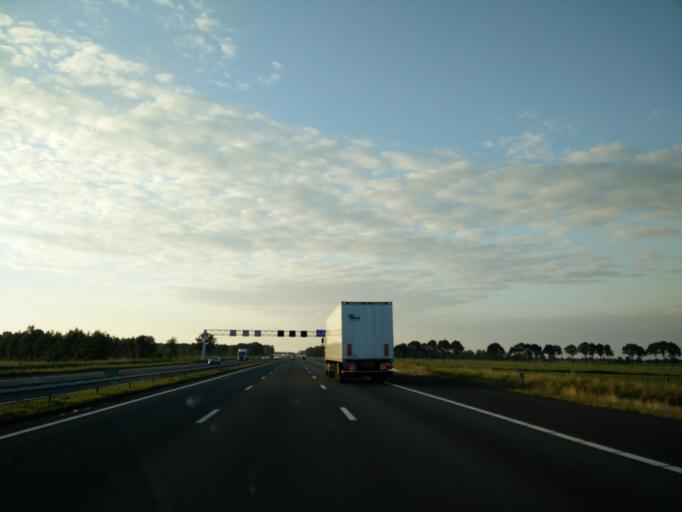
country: NL
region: Overijssel
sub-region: Gemeente Staphorst
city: Staphorst
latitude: 52.6119
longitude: 6.2073
